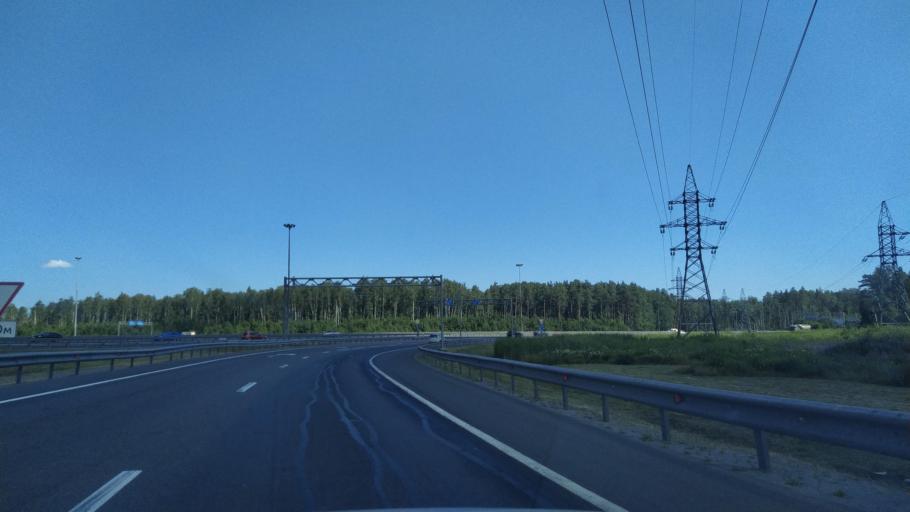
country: RU
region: Leningrad
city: Rybatskoye
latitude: 59.8916
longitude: 30.5273
